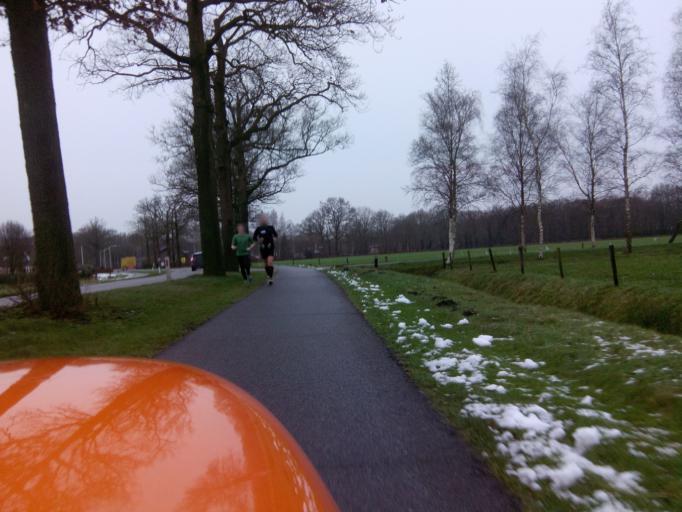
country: NL
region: Gelderland
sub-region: Gemeente Barneveld
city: Zwartebroek
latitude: 52.1937
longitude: 5.5299
